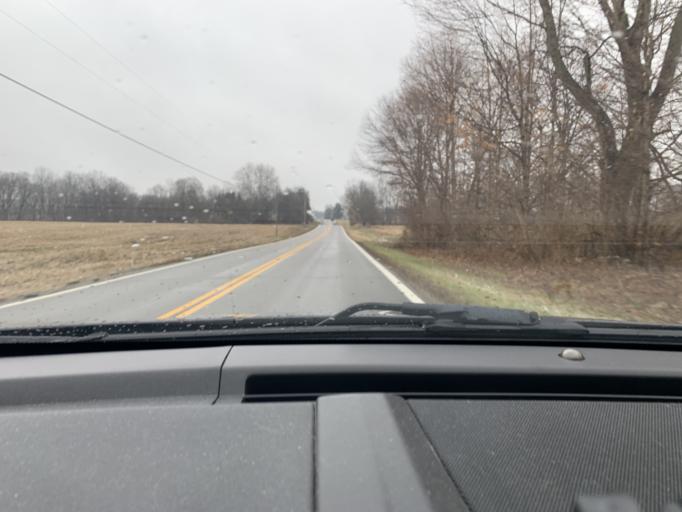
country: US
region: Ohio
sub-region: Ross County
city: Kingston
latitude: 39.4300
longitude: -82.9208
